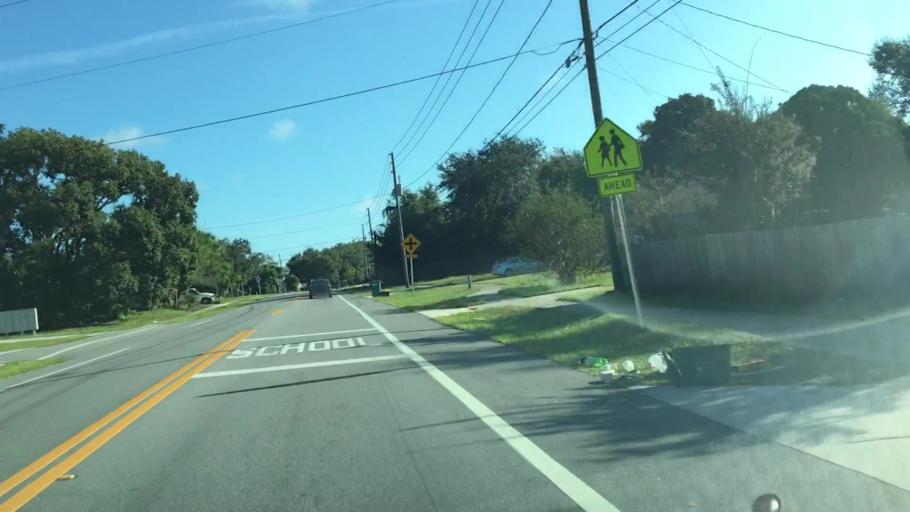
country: US
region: Florida
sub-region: Volusia County
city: Deltona
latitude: 28.8716
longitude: -81.2422
